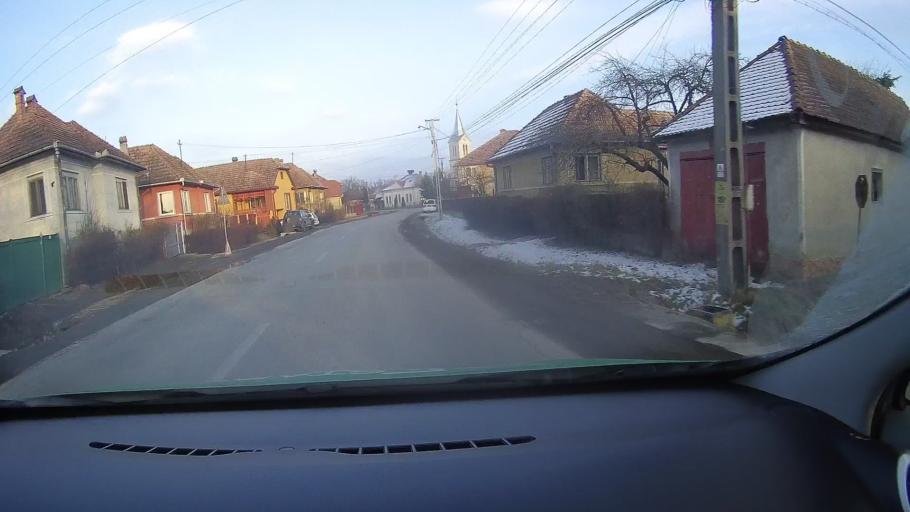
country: RO
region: Harghita
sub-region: Oras Cristuru Secuiesc
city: Filias
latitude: 46.2747
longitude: 24.9969
